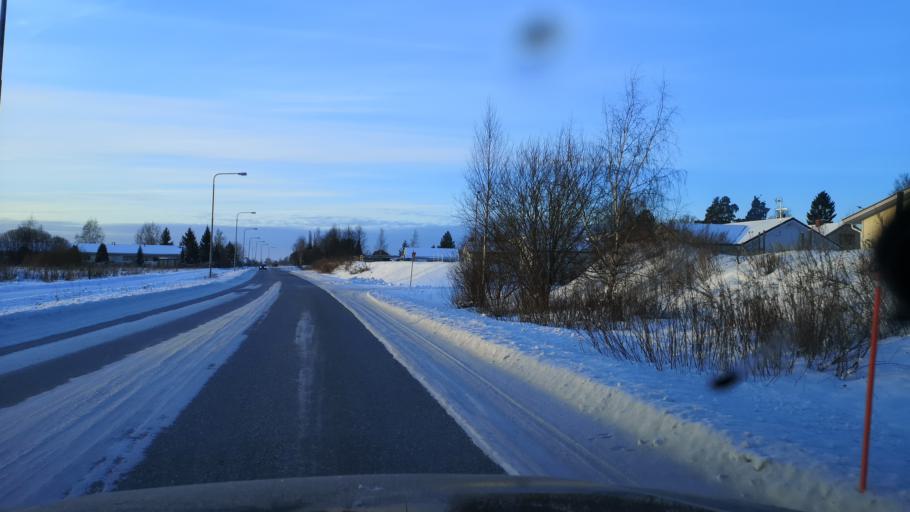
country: FI
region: Satakunta
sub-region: Pori
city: Pori
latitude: 61.5038
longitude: 21.8466
